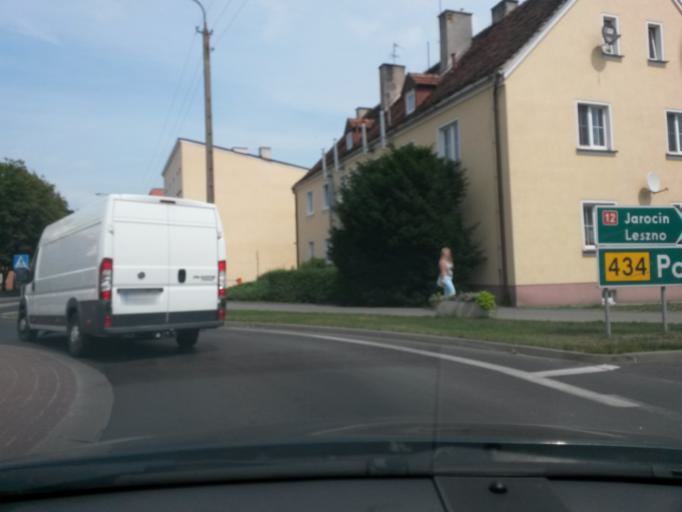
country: PL
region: Greater Poland Voivodeship
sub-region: Powiat gostynski
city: Gostyn
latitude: 51.8772
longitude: 17.0118
